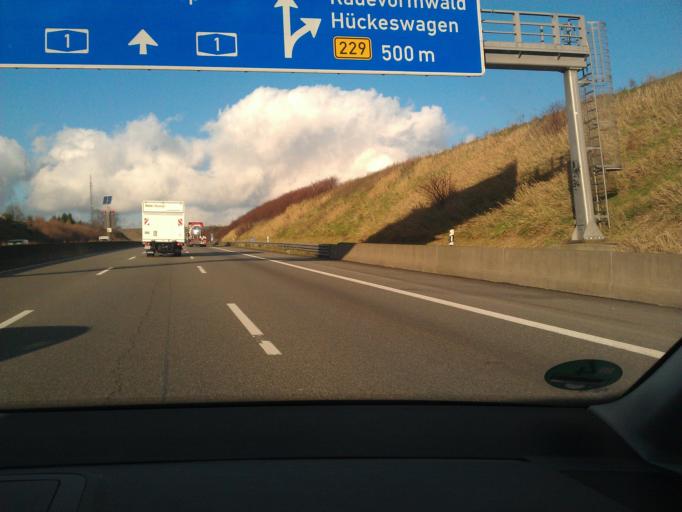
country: DE
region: North Rhine-Westphalia
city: Wermelskirchen
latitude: 51.1760
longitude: 7.2382
